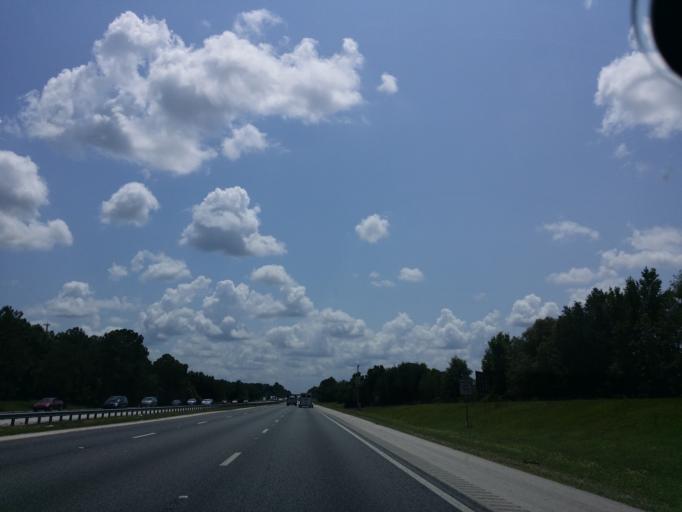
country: US
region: Florida
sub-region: Marion County
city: Ocala
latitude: 29.1312
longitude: -82.1849
